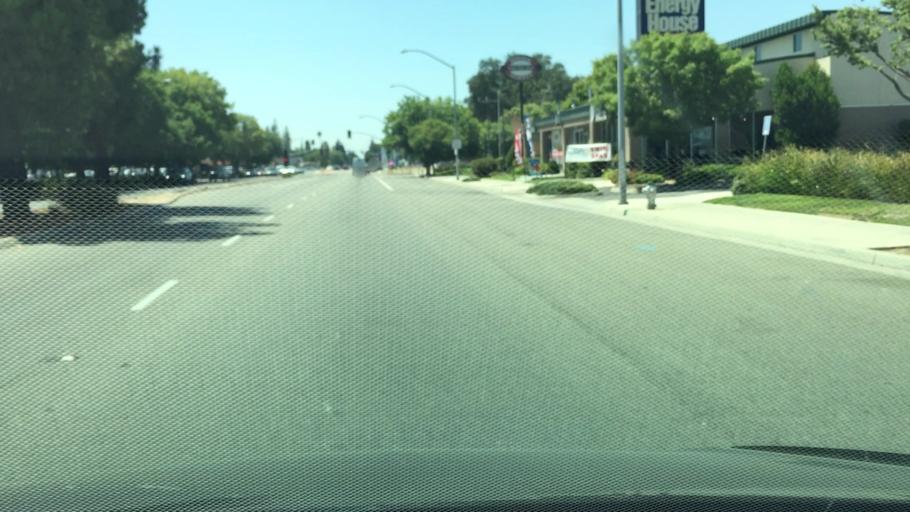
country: US
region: California
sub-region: Fresno County
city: Fresno
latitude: 36.8230
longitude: -119.7868
